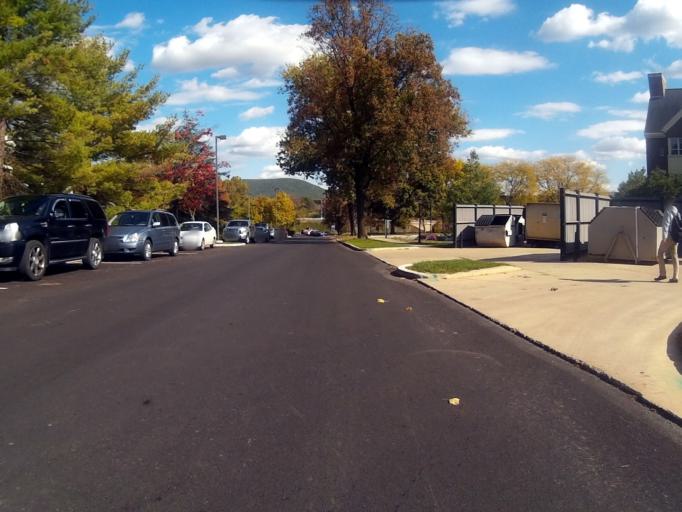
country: US
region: Pennsylvania
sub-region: Centre County
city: State College
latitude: 40.8027
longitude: -77.8533
